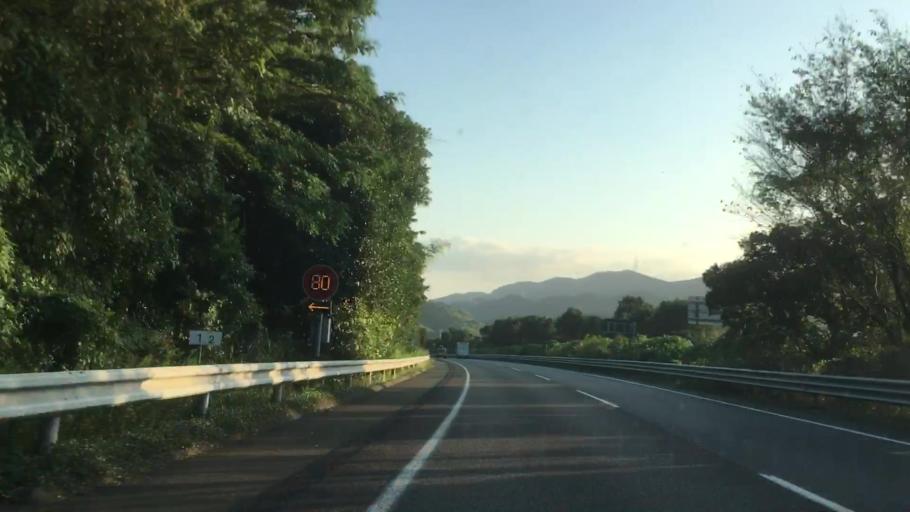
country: JP
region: Yamaguchi
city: Shimonoseki
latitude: 33.9154
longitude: 130.9765
